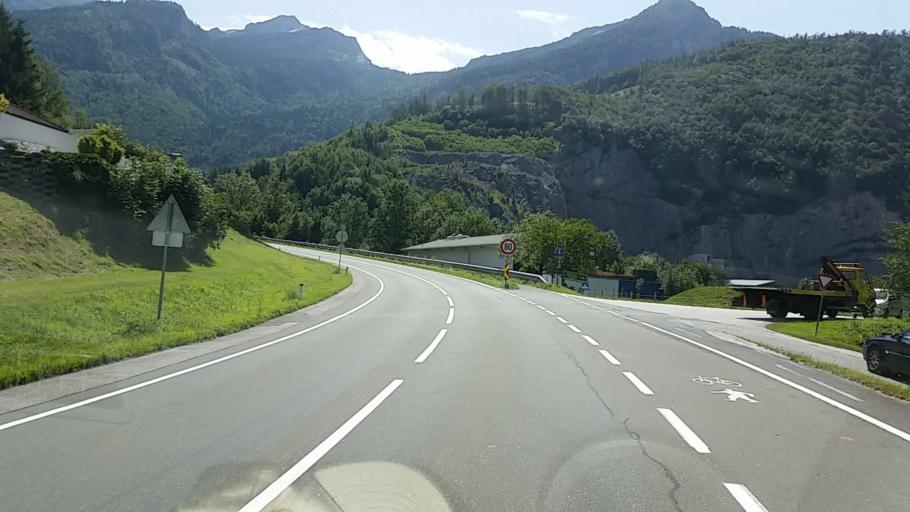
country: AT
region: Salzburg
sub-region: Politischer Bezirk Hallein
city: Golling an der Salzach
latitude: 47.5824
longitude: 13.1825
